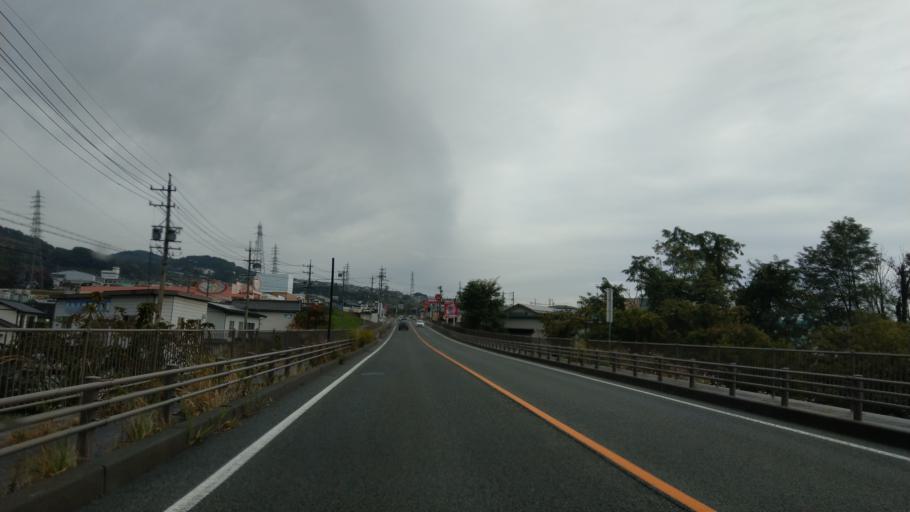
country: JP
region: Nagano
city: Komoro
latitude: 36.3371
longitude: 138.4139
